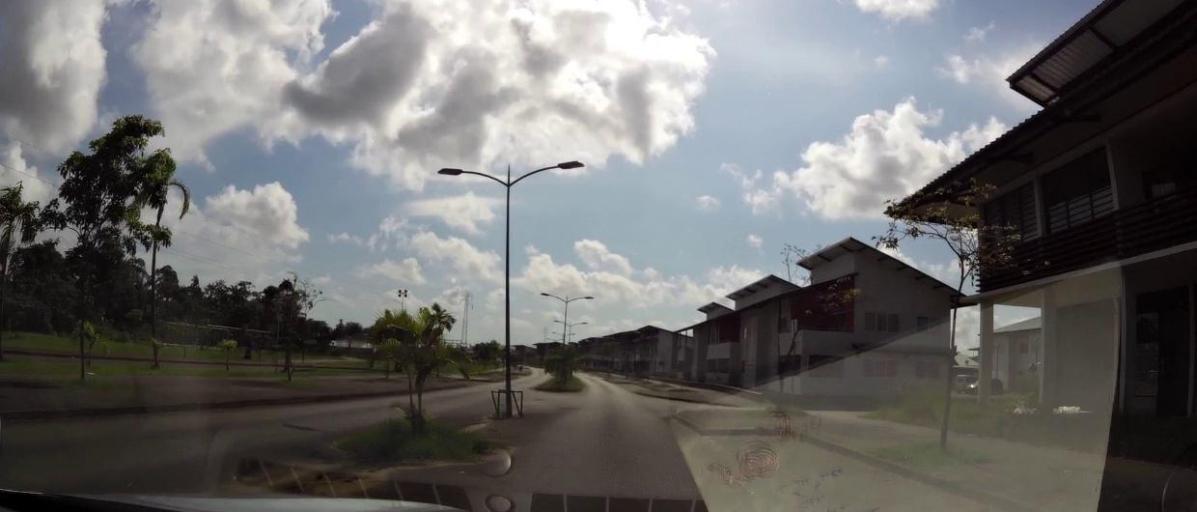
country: GF
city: Macouria
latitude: 4.9236
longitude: -52.4178
